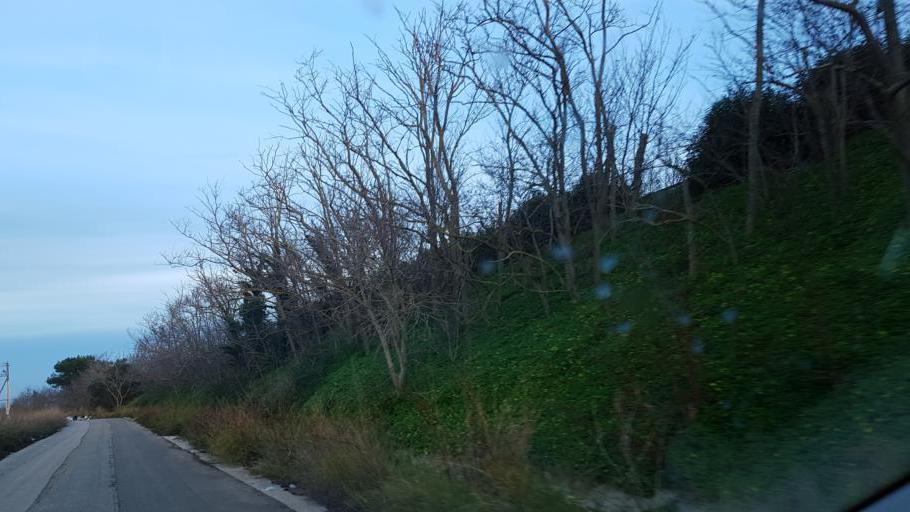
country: IT
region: Apulia
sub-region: Provincia di Brindisi
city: Brindisi
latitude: 40.6591
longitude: 17.9101
